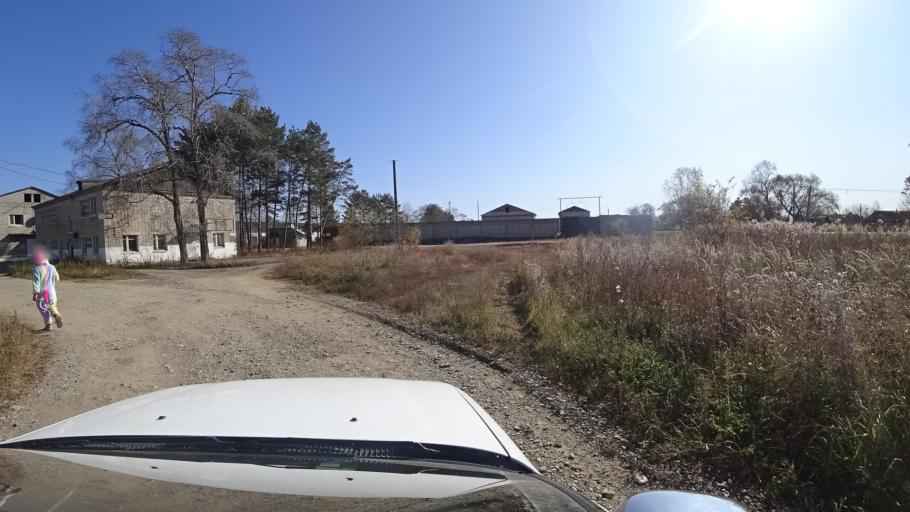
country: RU
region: Primorskiy
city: Dal'nerechensk
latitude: 45.9105
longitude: 133.8038
